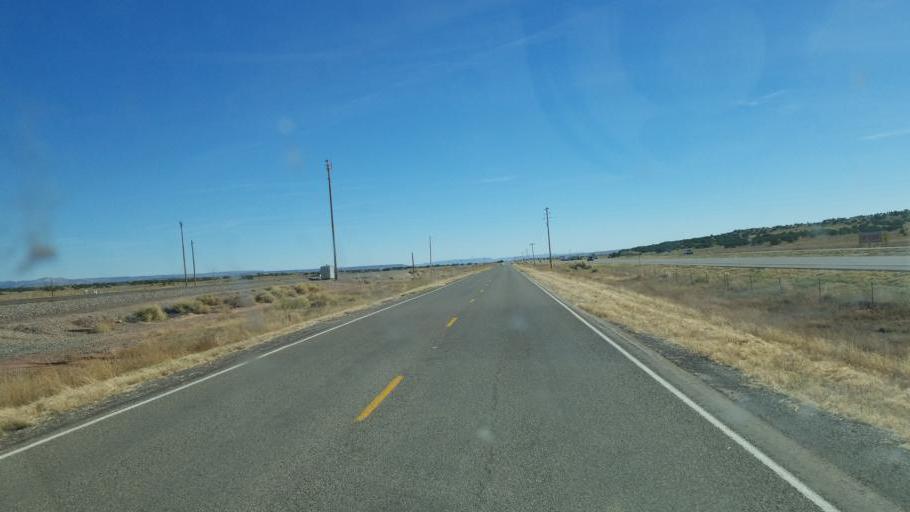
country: US
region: New Mexico
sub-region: Cibola County
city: Milan
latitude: 35.3288
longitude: -107.9995
